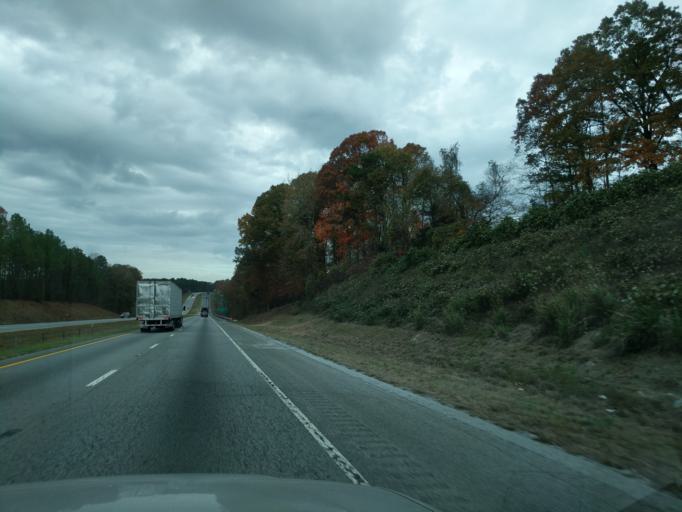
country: US
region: South Carolina
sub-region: Spartanburg County
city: Woodruff
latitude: 34.7283
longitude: -81.9498
